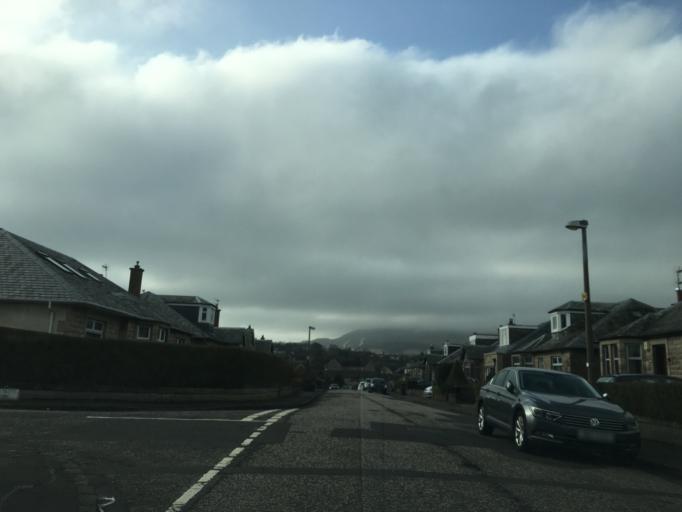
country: GB
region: Scotland
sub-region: Edinburgh
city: Colinton
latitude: 55.9139
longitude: -3.2216
